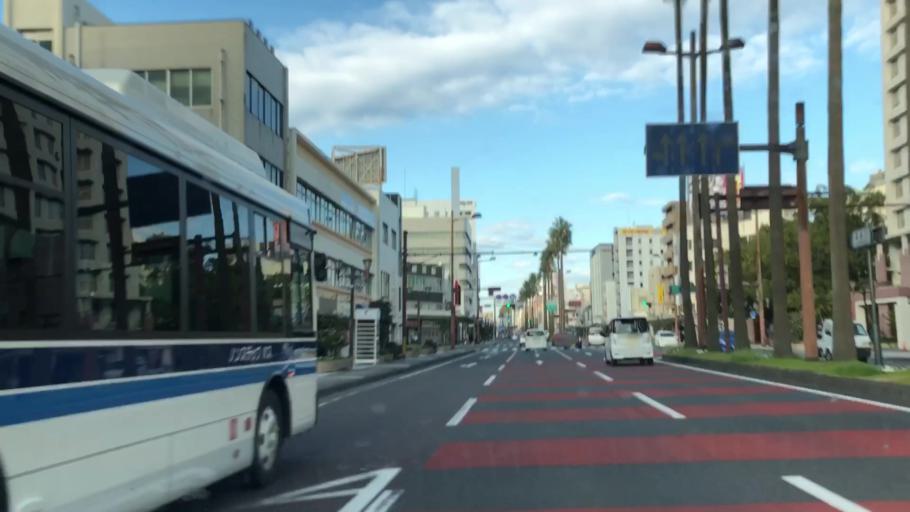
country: JP
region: Miyazaki
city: Miyazaki-shi
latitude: 31.9093
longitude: 131.4218
